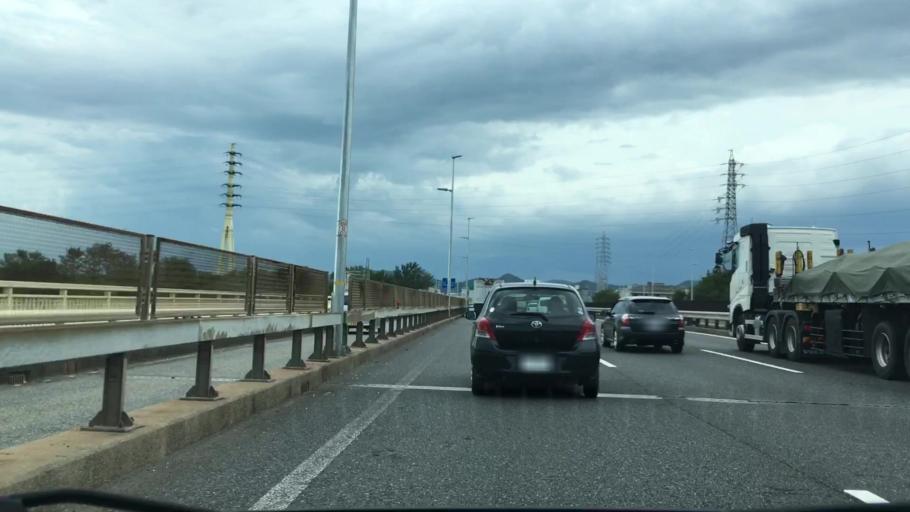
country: JP
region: Hyogo
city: Himeji
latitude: 34.8075
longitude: 134.6957
